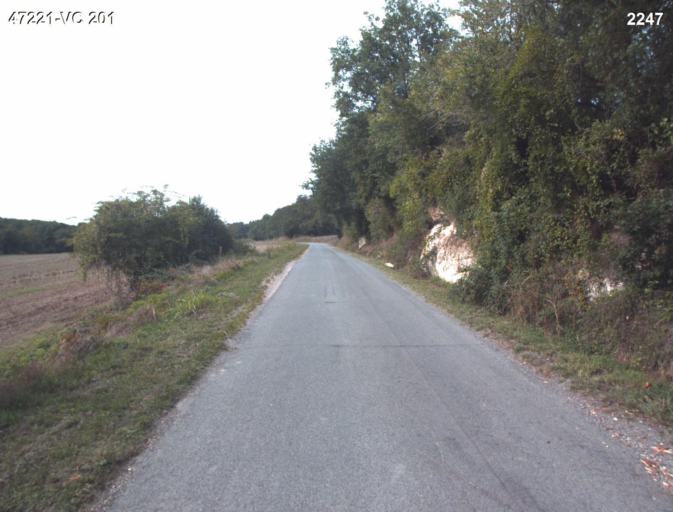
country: FR
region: Aquitaine
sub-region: Departement du Lot-et-Garonne
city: Mezin
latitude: 44.1096
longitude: 0.2460
